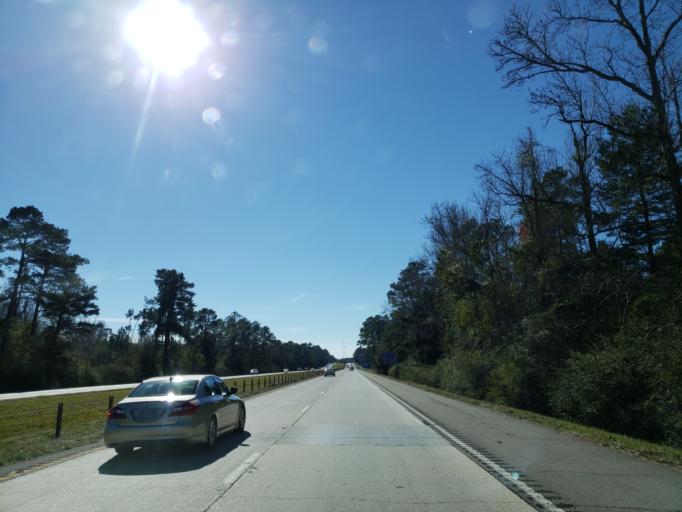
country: US
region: Mississippi
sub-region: Forrest County
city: Glendale
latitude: 31.3662
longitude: -89.3380
